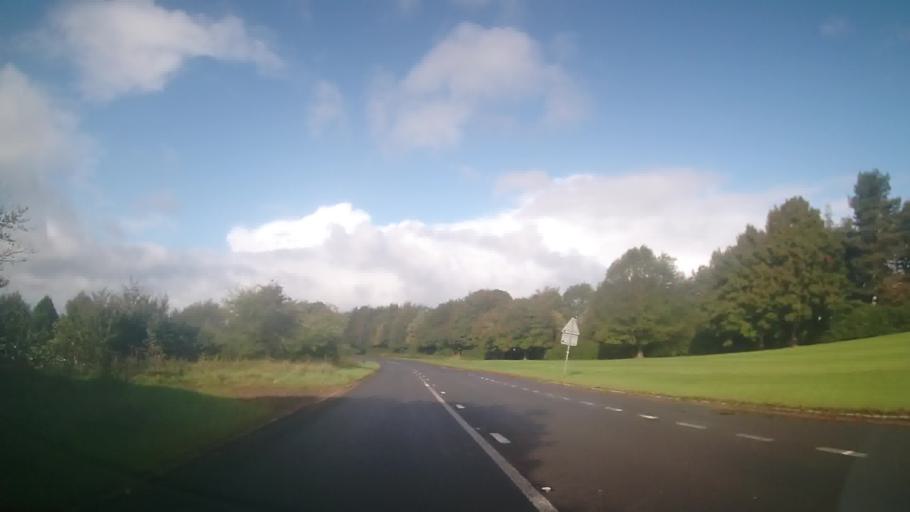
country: GB
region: England
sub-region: Gloucestershire
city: Moreton in Marsh
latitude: 51.9888
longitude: -1.6777
